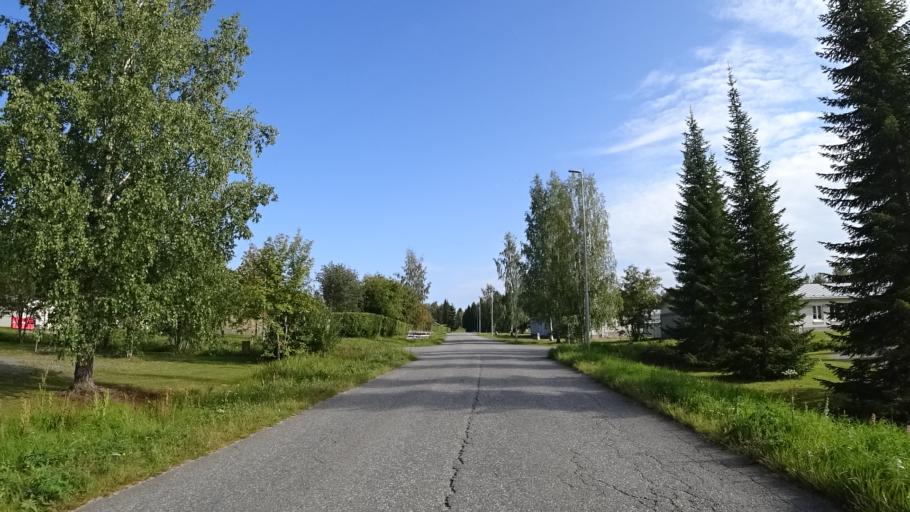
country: FI
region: North Karelia
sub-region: Joensuu
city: Eno
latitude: 62.7954
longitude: 30.1396
